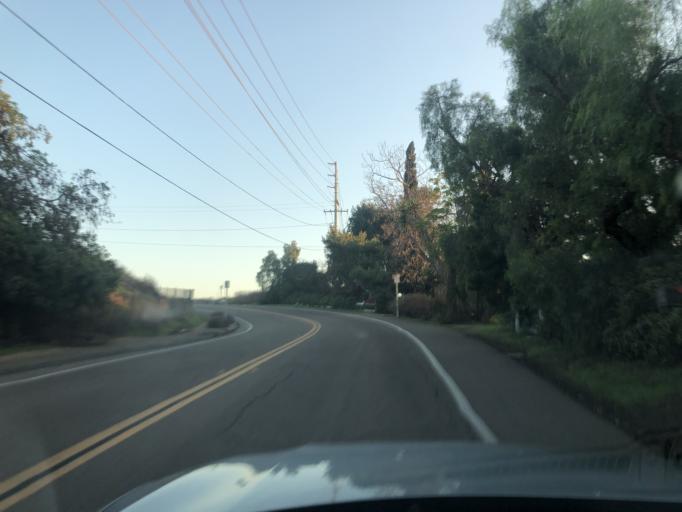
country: US
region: California
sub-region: San Diego County
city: Chula Vista
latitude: 32.6465
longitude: -117.0569
